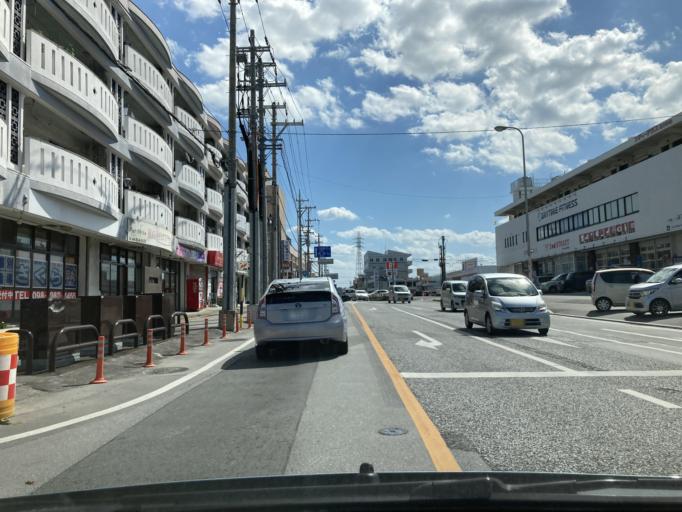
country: JP
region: Okinawa
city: Tomigusuku
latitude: 26.1922
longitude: 127.7073
